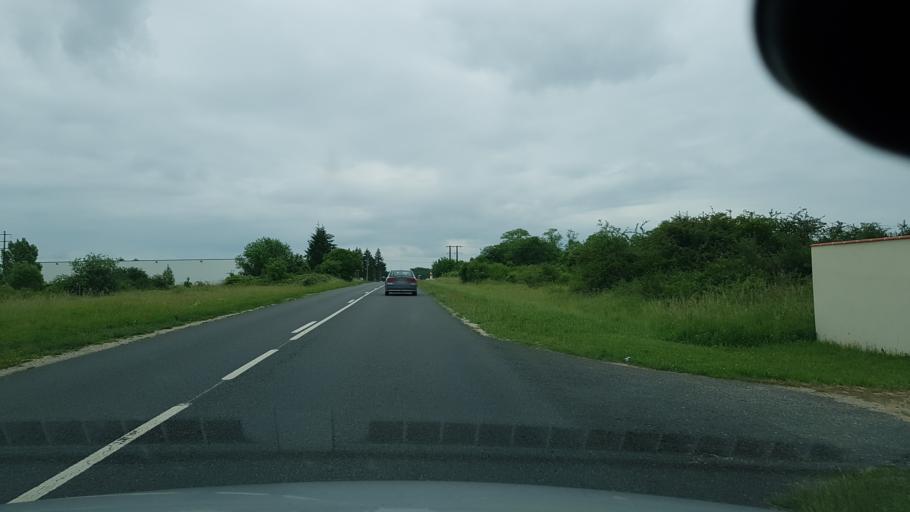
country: FR
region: Centre
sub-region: Departement du Loir-et-Cher
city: Selles-sur-Cher
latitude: 47.2938
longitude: 1.5241
